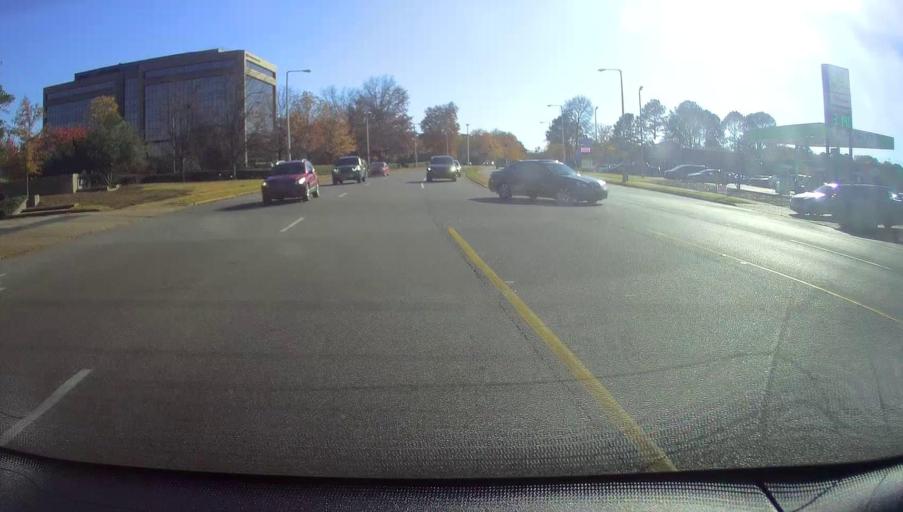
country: US
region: Tennessee
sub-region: Shelby County
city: Germantown
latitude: 35.1003
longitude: -89.8391
